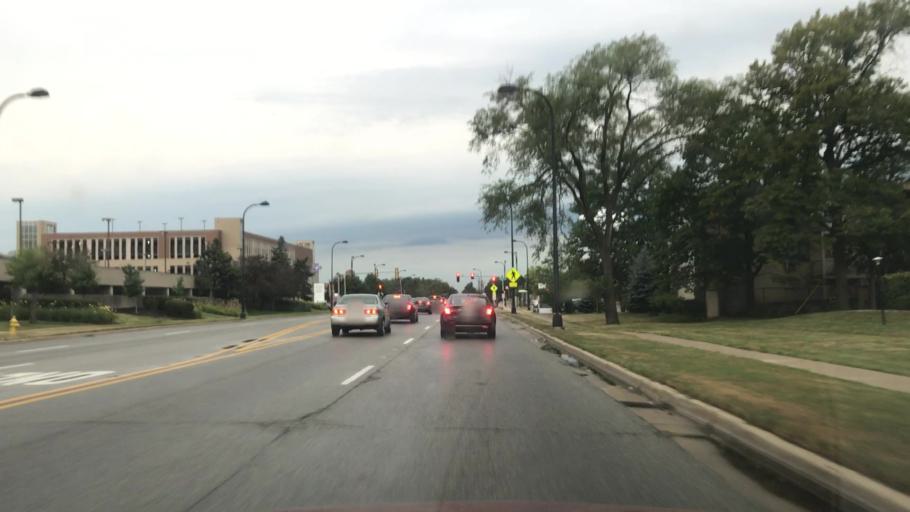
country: US
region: Illinois
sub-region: Cook County
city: Park Ridge
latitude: 42.0398
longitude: -87.8478
